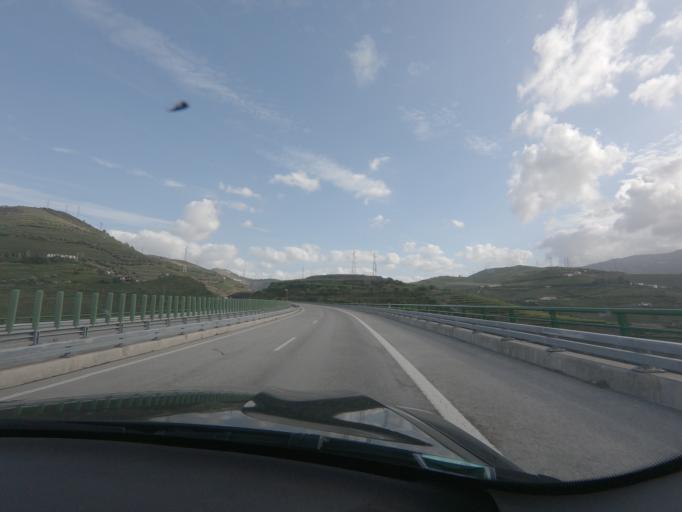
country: PT
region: Vila Real
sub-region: Peso da Regua
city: Peso da Regua
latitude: 41.1535
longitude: -7.7773
